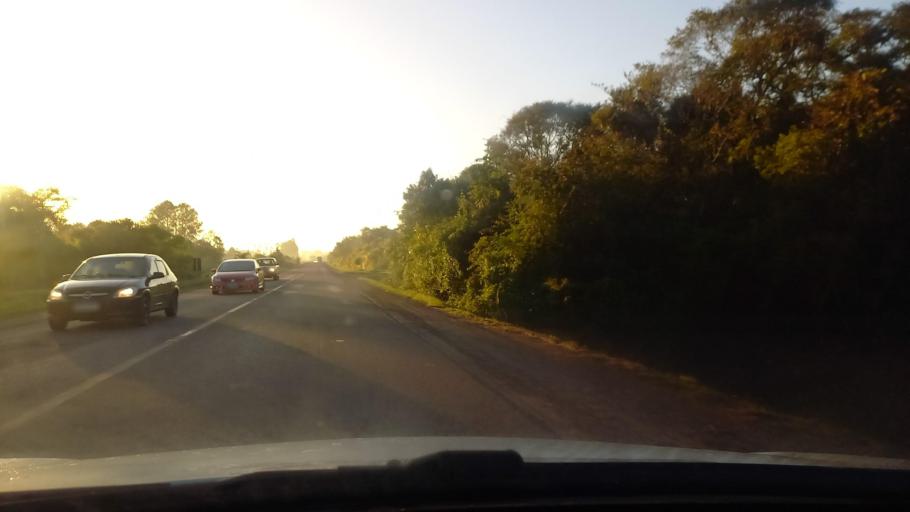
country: BR
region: Rio Grande do Sul
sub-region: Candelaria
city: Candelaria
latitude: -29.6808
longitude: -52.8332
